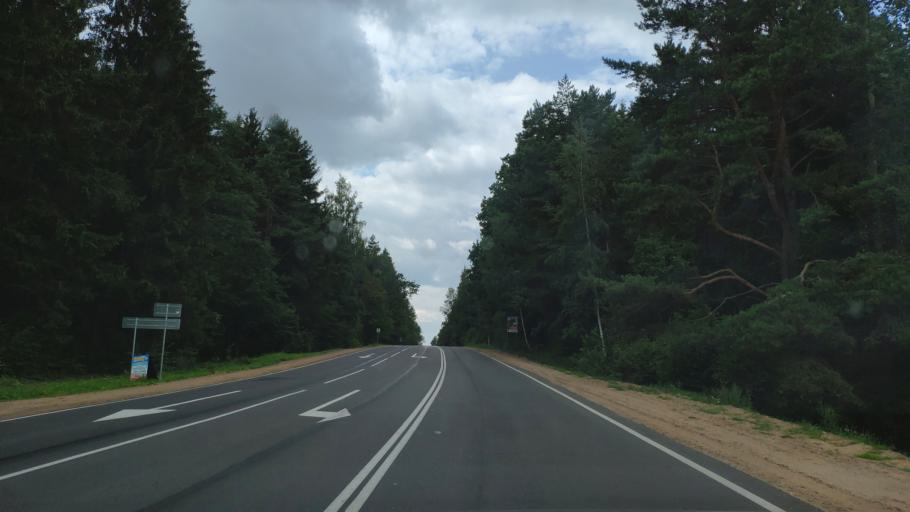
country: BY
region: Minsk
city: Syomkava
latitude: 54.0097
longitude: 27.4176
